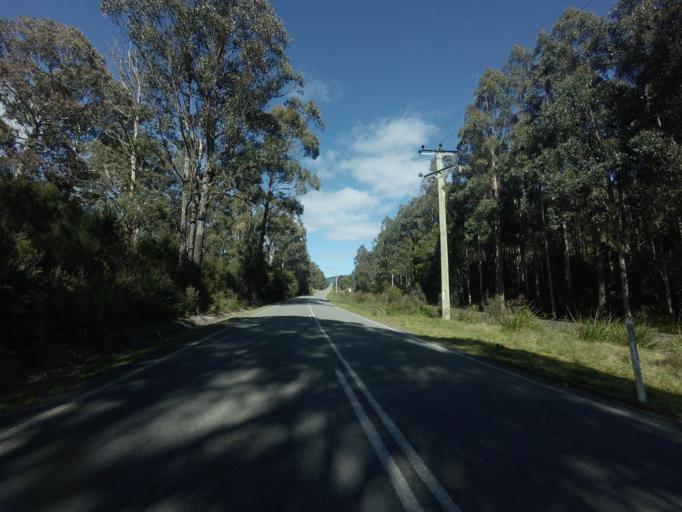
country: AU
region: Tasmania
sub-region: Derwent Valley
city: New Norfolk
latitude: -42.7168
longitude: 146.6908
